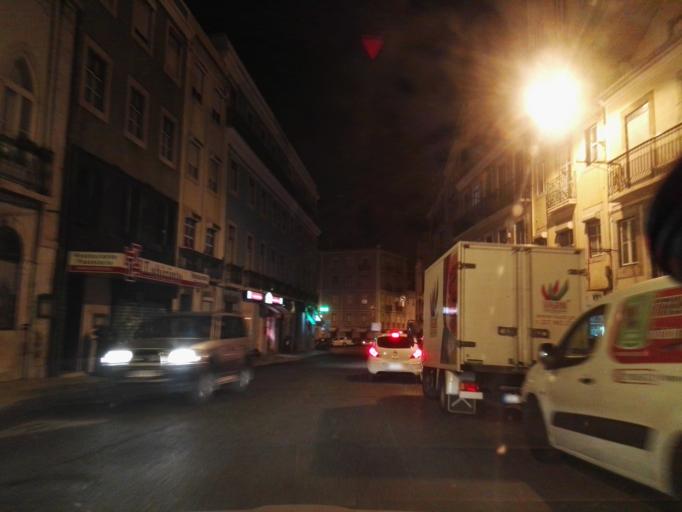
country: PT
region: Lisbon
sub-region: Lisbon
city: Lisbon
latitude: 38.7196
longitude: -9.1378
